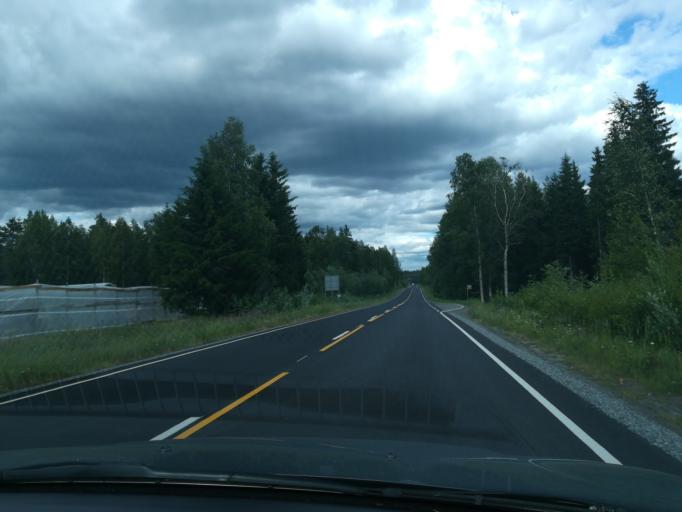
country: FI
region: Southern Savonia
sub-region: Mikkeli
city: Mikkeli
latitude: 61.6530
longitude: 27.0936
